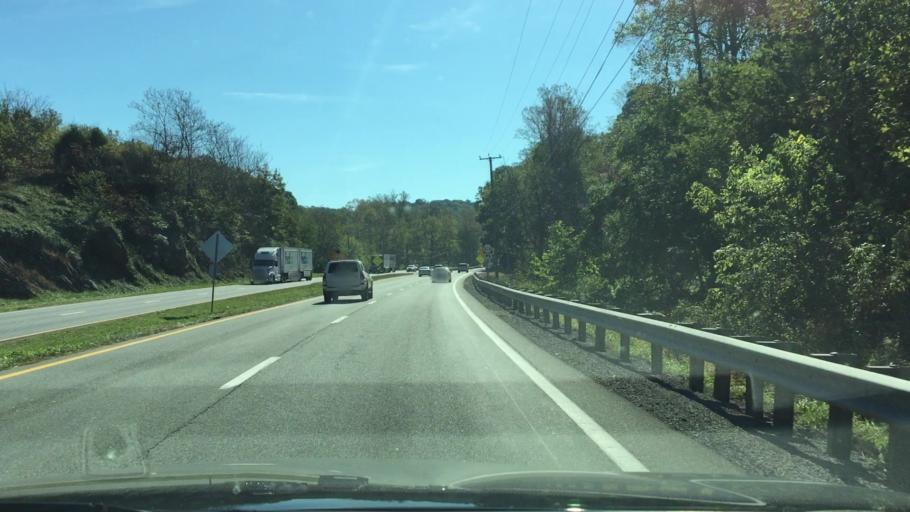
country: US
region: Virginia
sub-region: Roanoke County
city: Narrows
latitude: 37.1273
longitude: -79.9618
